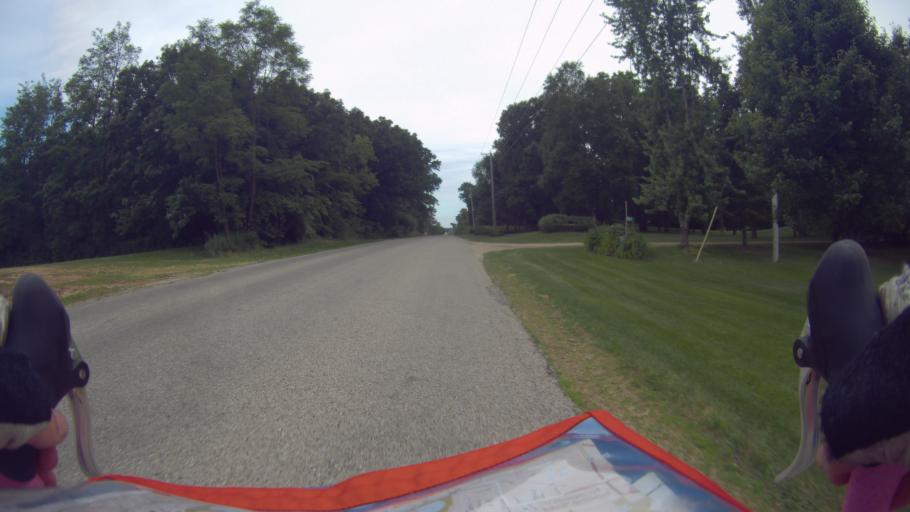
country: US
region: Wisconsin
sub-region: Dane County
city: Oregon
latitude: 42.9458
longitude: -89.3484
